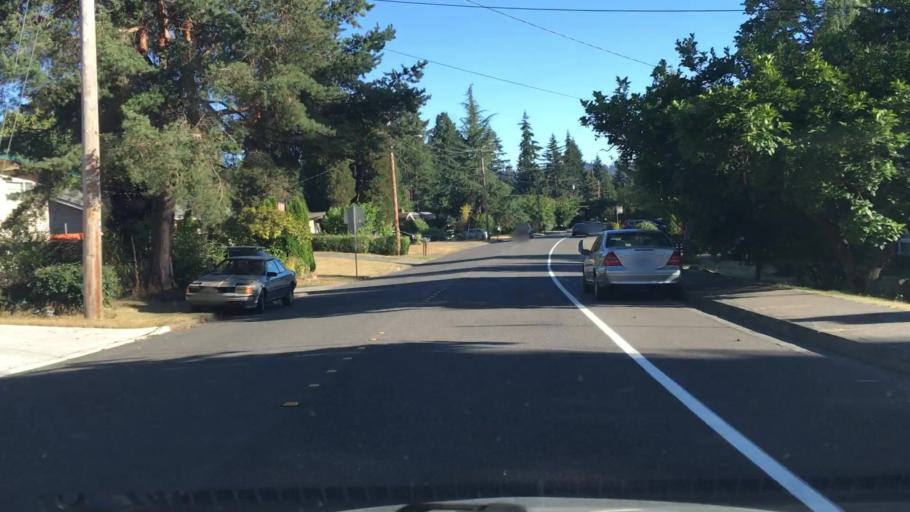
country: US
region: Washington
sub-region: King County
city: West Lake Sammamish
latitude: 47.6020
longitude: -122.1213
